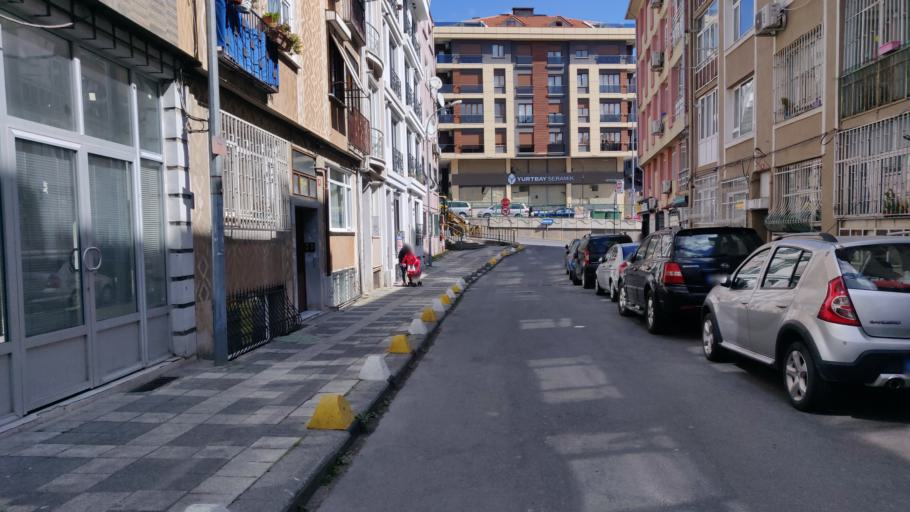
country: TR
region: Istanbul
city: UEskuedar
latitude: 40.9953
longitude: 29.0373
